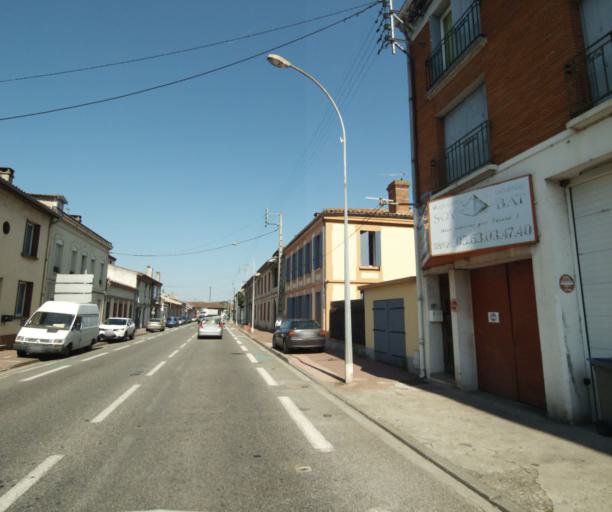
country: FR
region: Midi-Pyrenees
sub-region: Departement du Tarn-et-Garonne
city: Montauban
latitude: 44.0129
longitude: 1.3454
